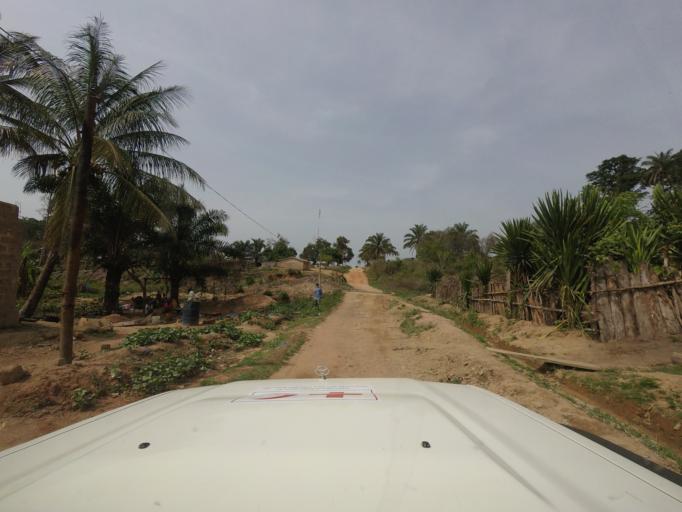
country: GN
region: Nzerekore
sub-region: Macenta
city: Macenta
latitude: 8.4552
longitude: -9.5877
